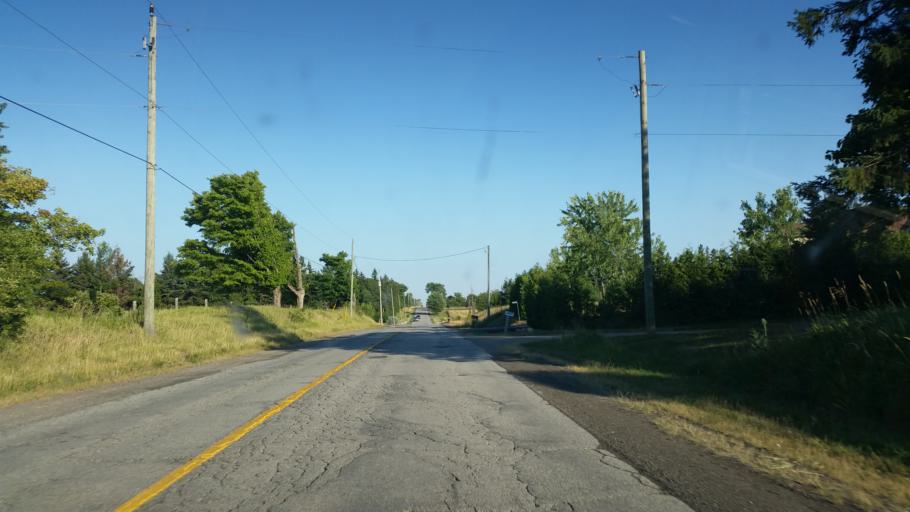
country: CA
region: Ontario
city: Brampton
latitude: 43.7695
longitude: -79.8260
